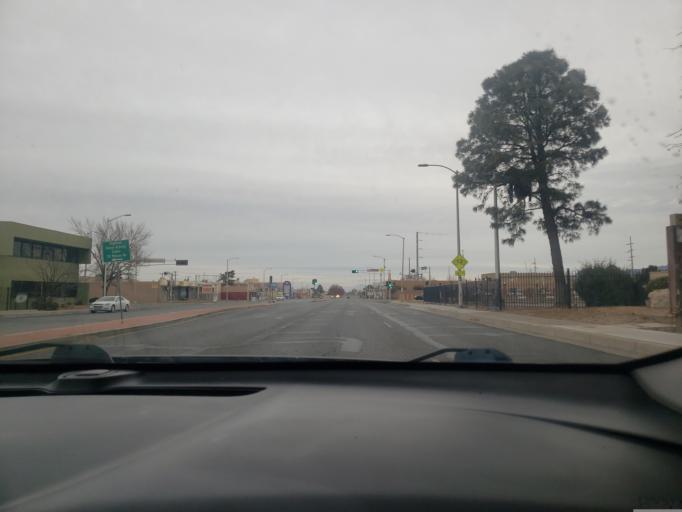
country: US
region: New Mexico
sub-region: Bernalillo County
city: Albuquerque
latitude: 35.0798
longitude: -106.5861
